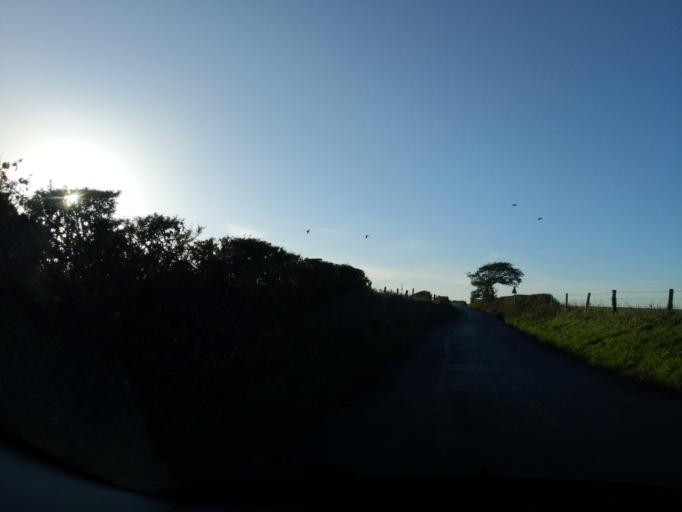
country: GB
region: England
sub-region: Plymouth
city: Plymstock
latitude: 50.3434
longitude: -4.0959
